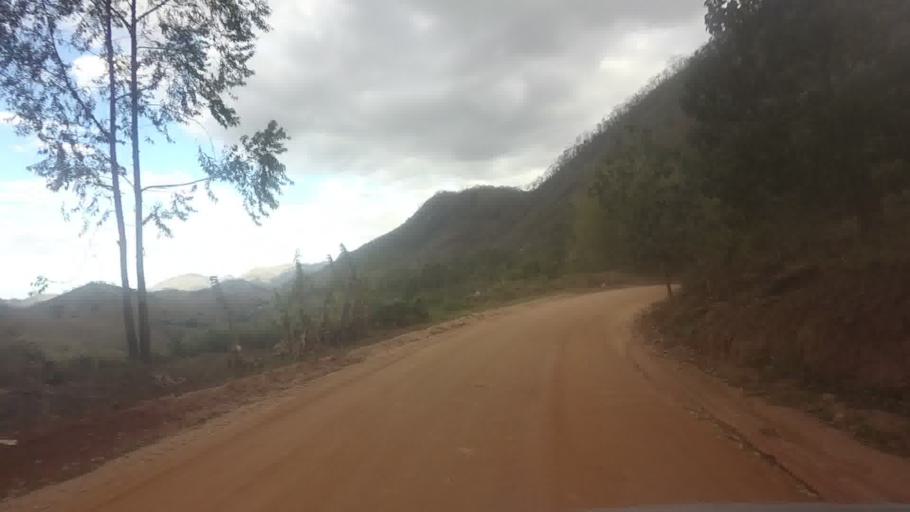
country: BR
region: Espirito Santo
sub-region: Mimoso Do Sul
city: Mimoso do Sul
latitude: -20.9460
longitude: -41.3960
